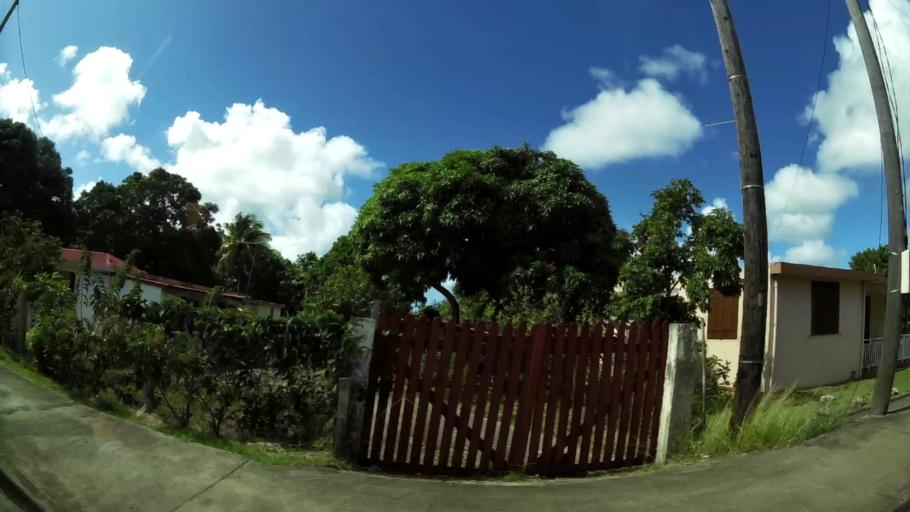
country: GP
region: Guadeloupe
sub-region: Guadeloupe
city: Anse-Bertrand
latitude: 16.4411
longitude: -61.4748
